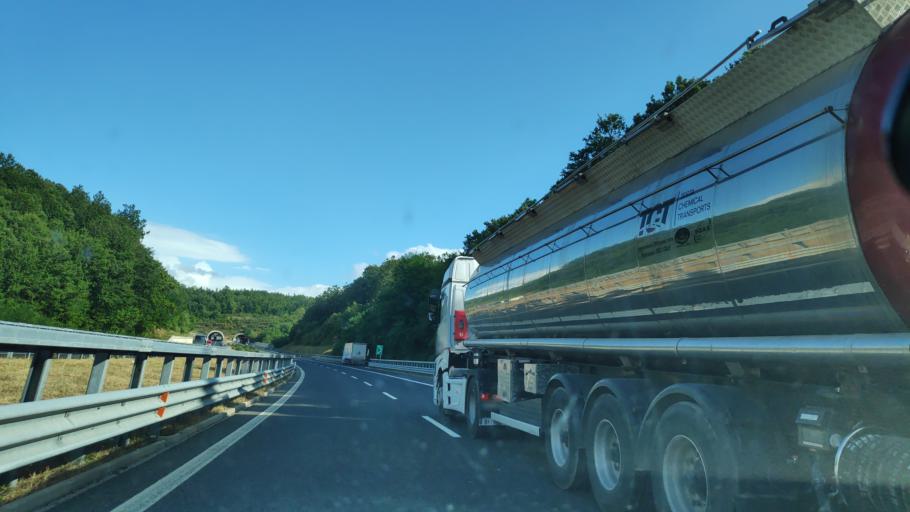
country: IT
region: Campania
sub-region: Provincia di Salerno
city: Casalbuono
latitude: 40.2382
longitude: 15.6604
